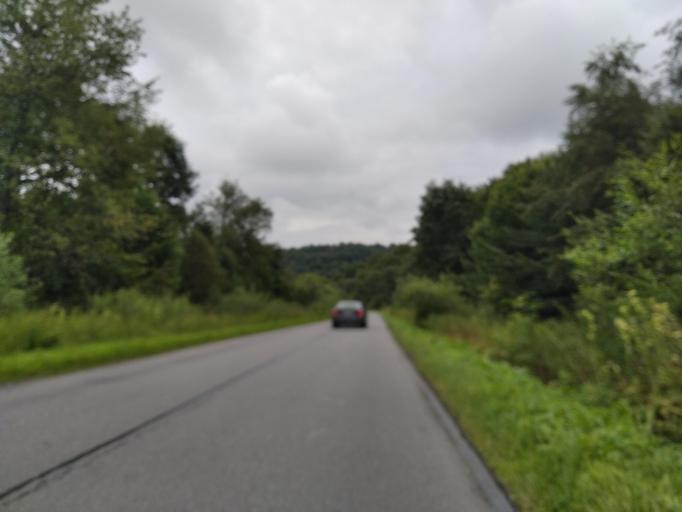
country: PL
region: Subcarpathian Voivodeship
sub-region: Powiat sanocki
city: Tyrawa Woloska
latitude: 49.6972
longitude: 22.3542
